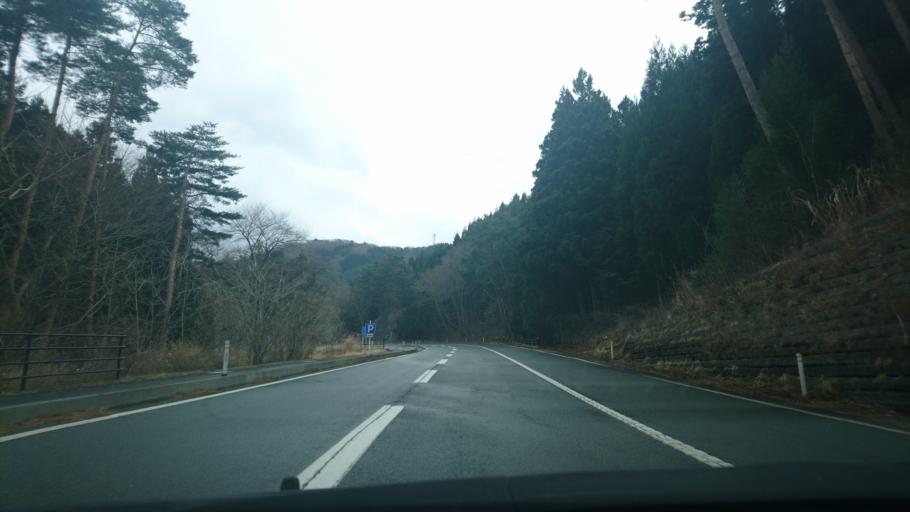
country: JP
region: Iwate
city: Ofunato
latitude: 39.1368
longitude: 141.8200
